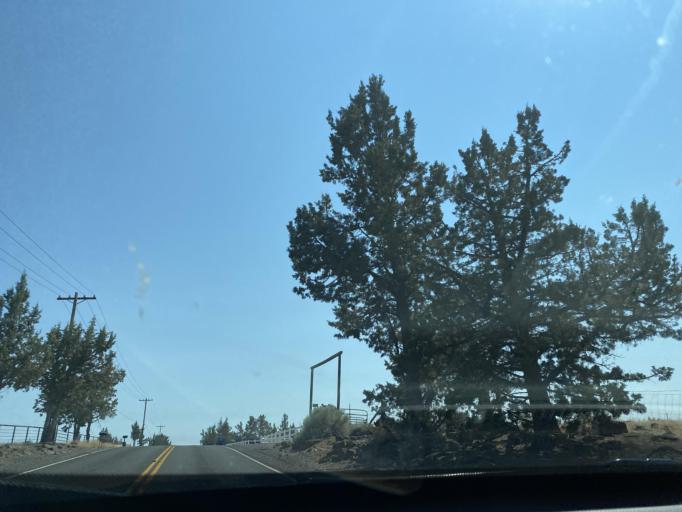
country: US
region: Oregon
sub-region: Deschutes County
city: Terrebonne
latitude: 44.3615
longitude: -121.1586
